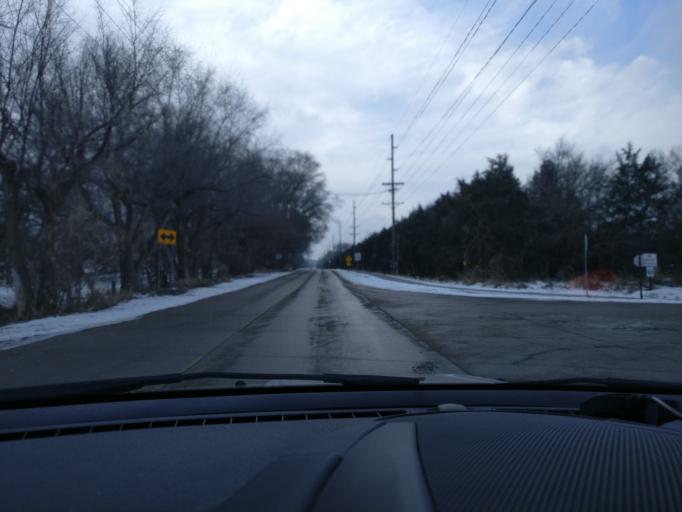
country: US
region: Nebraska
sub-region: Dodge County
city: Fremont
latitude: 41.4370
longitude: -96.5216
